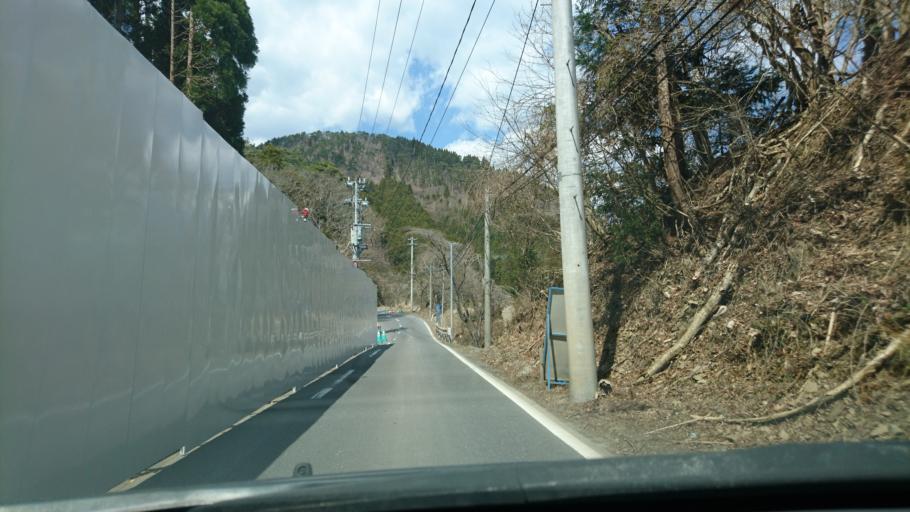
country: JP
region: Miyagi
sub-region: Oshika Gun
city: Onagawa Cho
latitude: 38.4419
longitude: 141.4846
